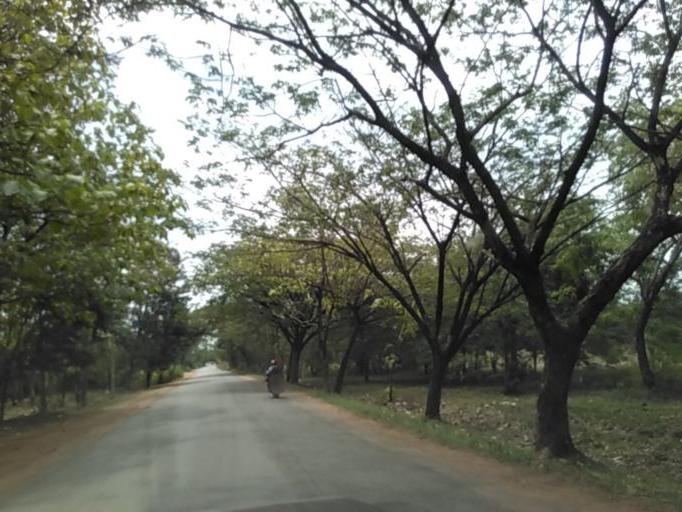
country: GH
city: Akropong
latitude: 6.0960
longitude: 0.1164
